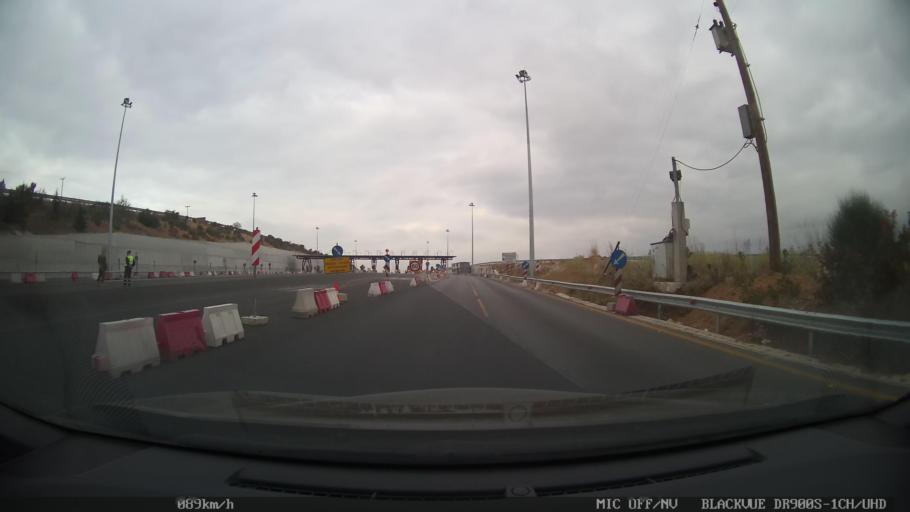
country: GR
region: Central Macedonia
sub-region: Nomos Thessalonikis
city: Evosmos
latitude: 40.6962
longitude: 22.8980
